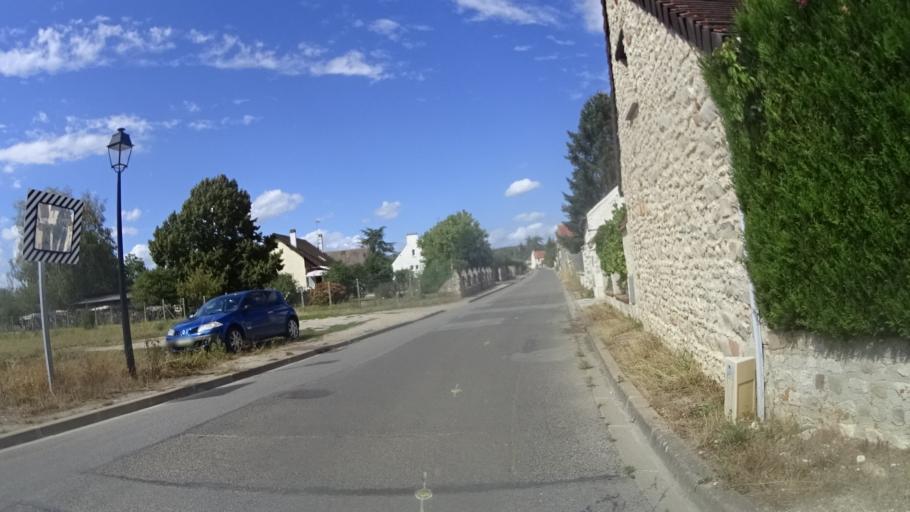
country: FR
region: Ile-de-France
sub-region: Departement de l'Essonne
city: Boutigny-sur-Essonne
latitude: 48.4174
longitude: 2.3909
